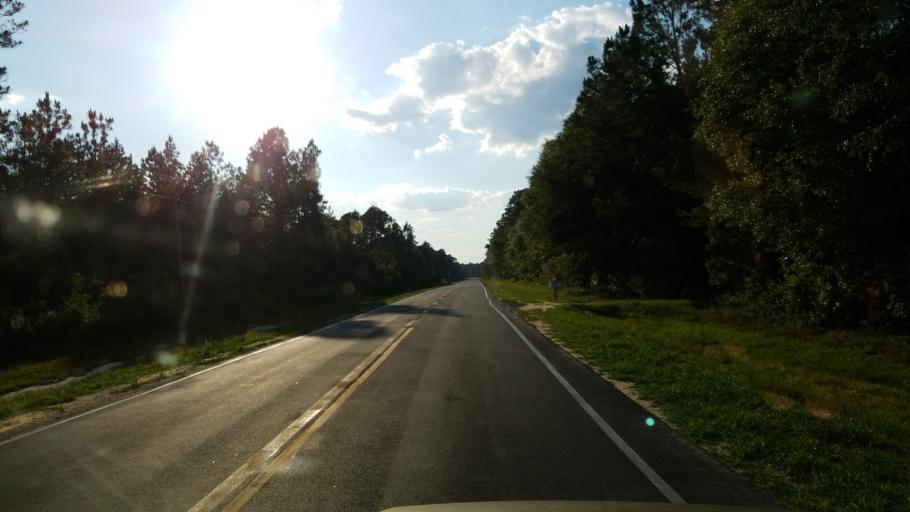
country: US
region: Georgia
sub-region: Berrien County
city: Nashville
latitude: 31.1805
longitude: -83.1385
